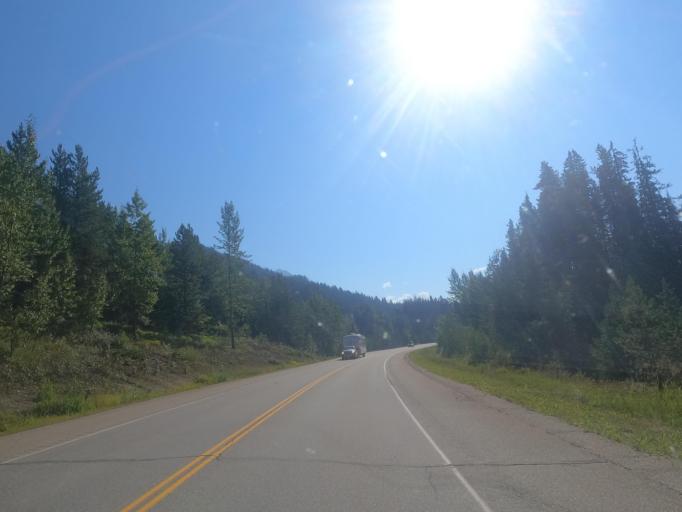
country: CA
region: Alberta
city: Jasper Park Lodge
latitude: 52.8925
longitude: -118.7329
